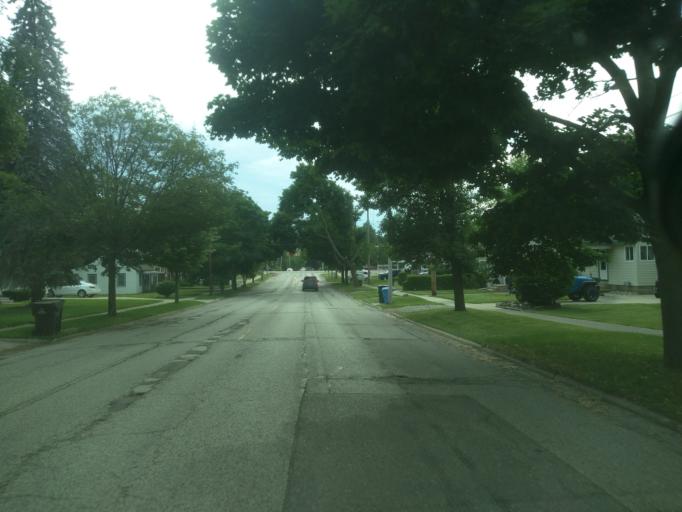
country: US
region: Michigan
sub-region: Ingham County
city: Lansing
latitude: 42.6902
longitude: -84.5459
